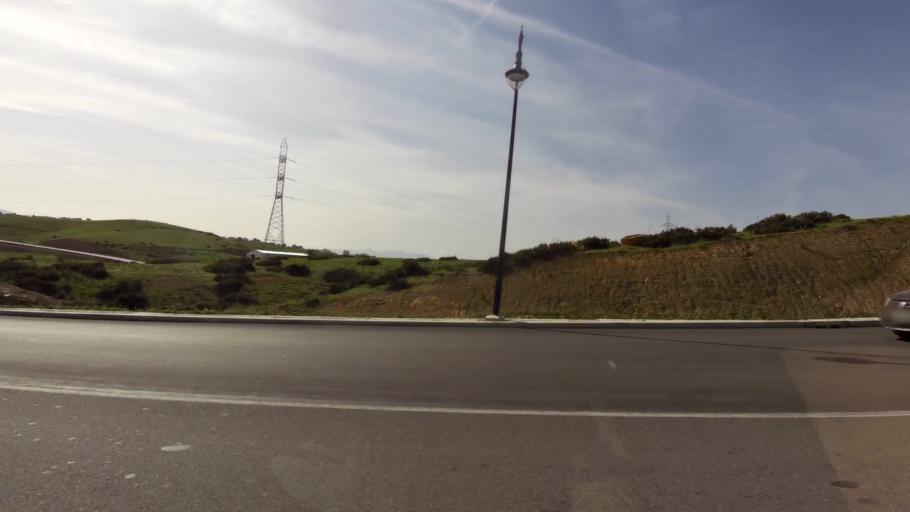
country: MA
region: Tanger-Tetouan
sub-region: Tanger-Assilah
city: Tangier
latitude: 35.7058
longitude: -5.7911
